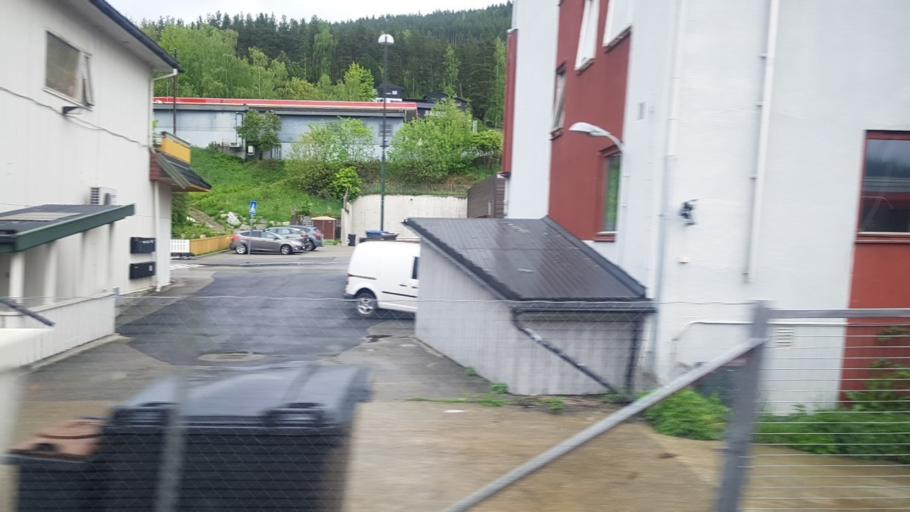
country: NO
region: Oppland
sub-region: Nord-Fron
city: Vinstra
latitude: 61.5951
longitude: 9.7341
